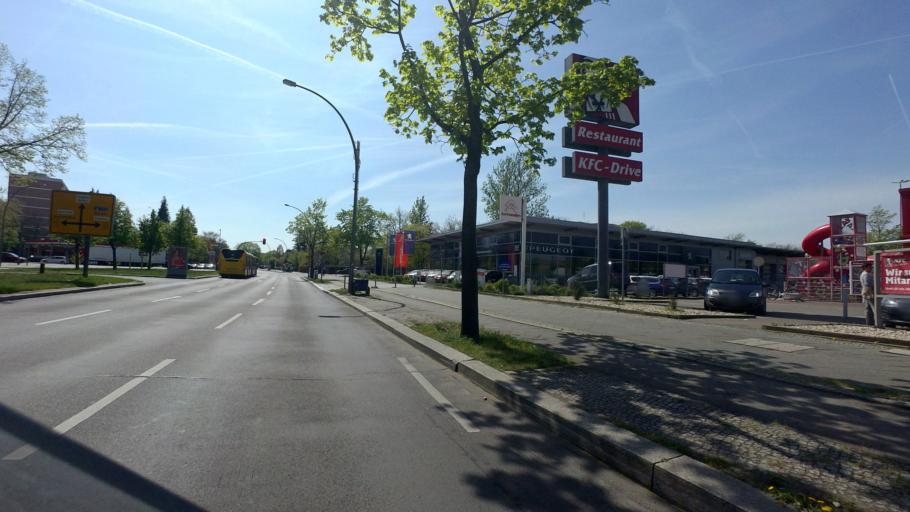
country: DE
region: Berlin
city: Wilhelmstadt
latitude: 52.5164
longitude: 13.1851
